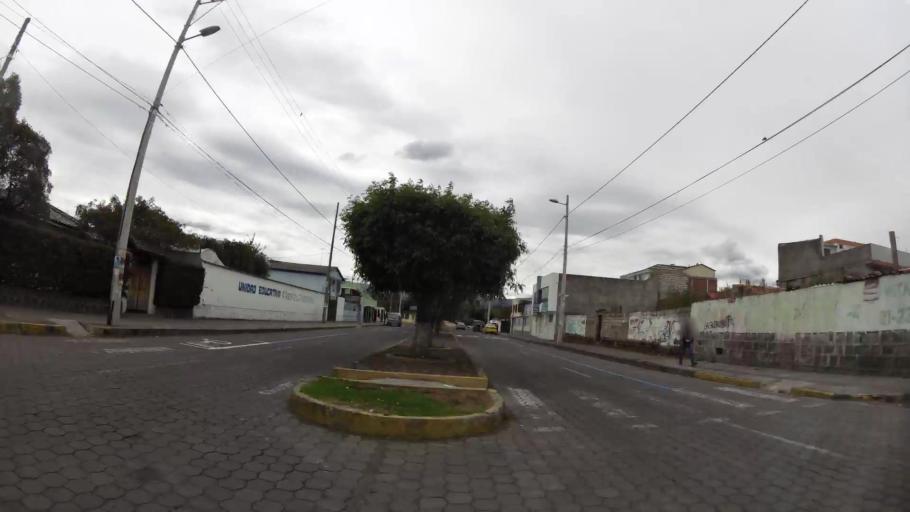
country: EC
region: Cotopaxi
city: Latacunga
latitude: -0.9402
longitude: -78.6130
